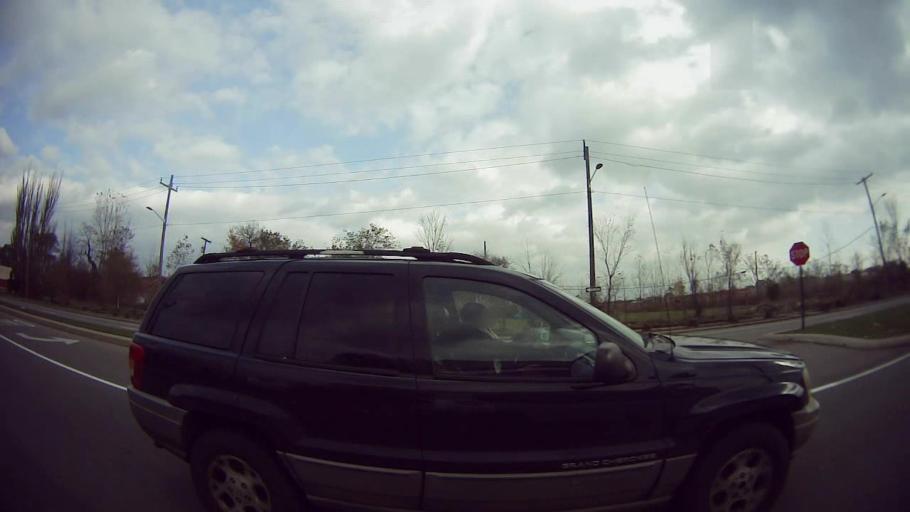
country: US
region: Michigan
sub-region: Wayne County
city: Highland Park
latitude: 42.3974
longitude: -83.1401
